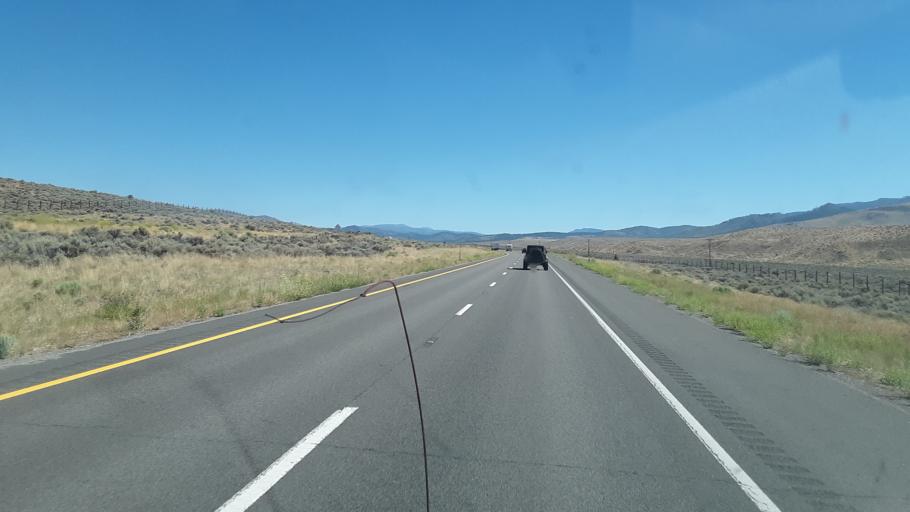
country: US
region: Nevada
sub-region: Washoe County
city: Cold Springs
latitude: 39.7208
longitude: -120.0383
